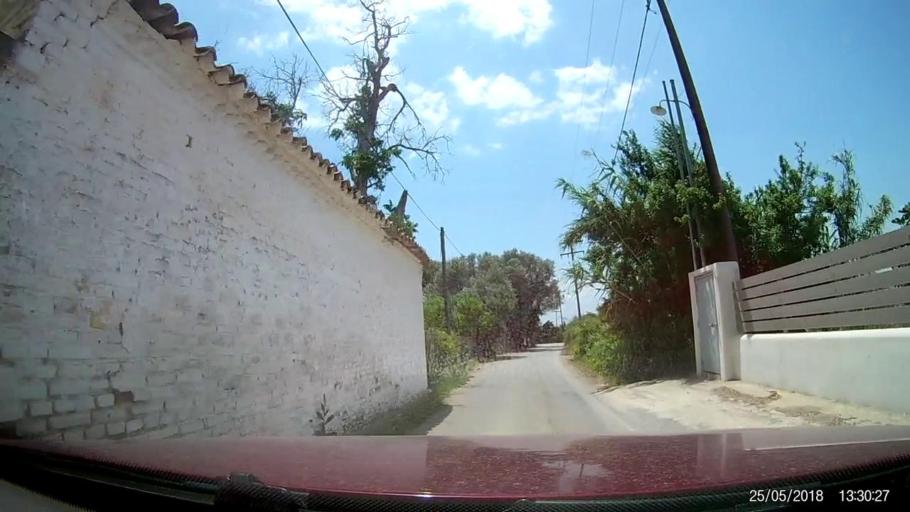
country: GR
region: Central Greece
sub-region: Nomos Evvoias
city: Mytikas
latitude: 38.4409
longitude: 23.6576
